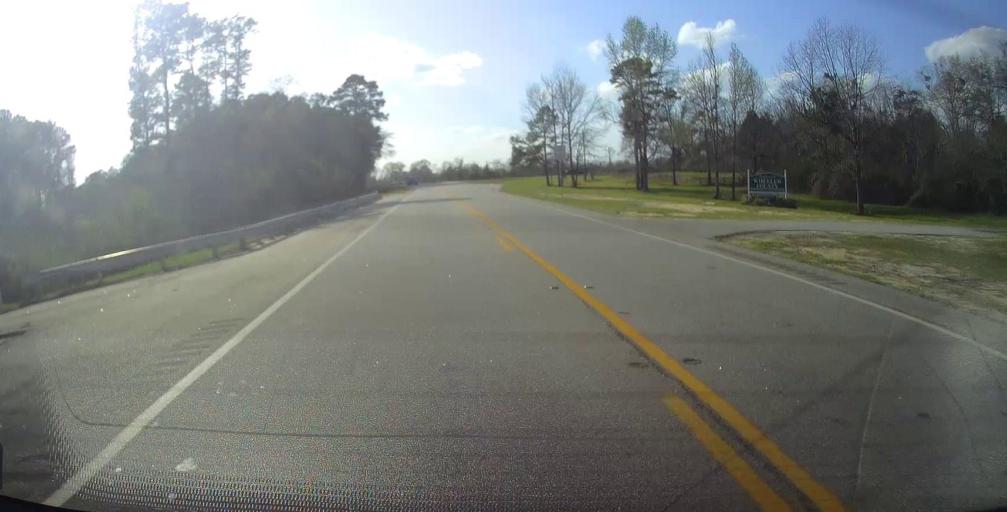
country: US
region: Georgia
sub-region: Montgomery County
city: Mount Vernon
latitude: 32.1909
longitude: -82.6346
